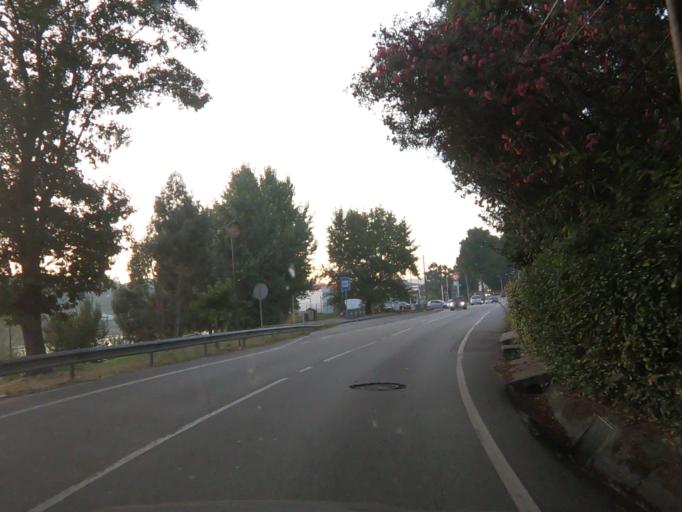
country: PT
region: Porto
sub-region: Gondomar
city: Valbom
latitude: 41.1271
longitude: -8.5655
